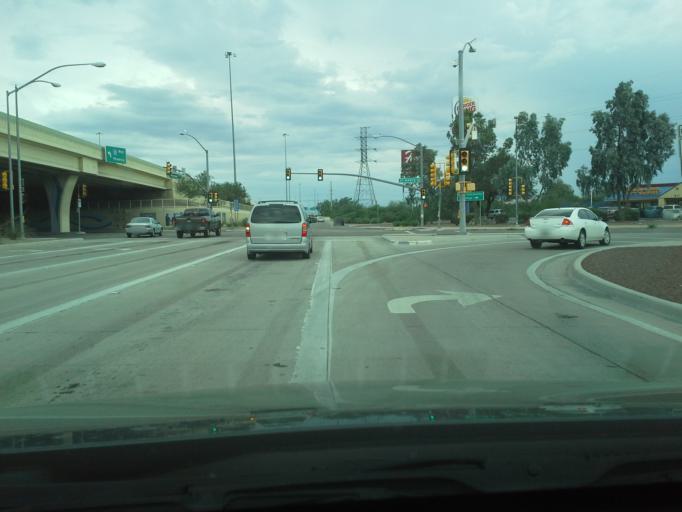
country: US
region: Arizona
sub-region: Pima County
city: South Tucson
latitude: 32.2299
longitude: -110.9831
